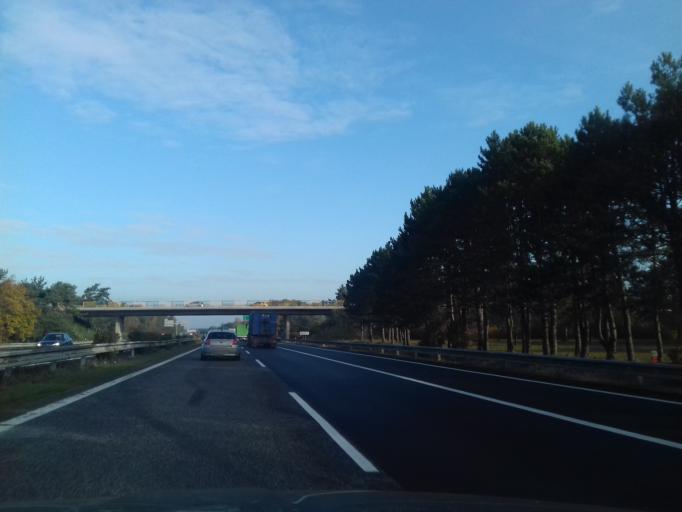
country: SK
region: Bratislavsky
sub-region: Okres Malacky
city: Malacky
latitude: 48.4267
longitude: 17.0421
